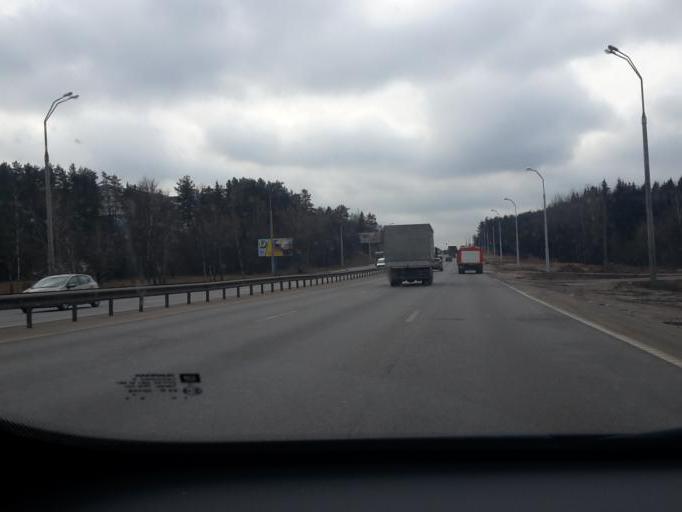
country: BY
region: Minsk
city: Borovlyany
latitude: 53.9312
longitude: 27.6770
